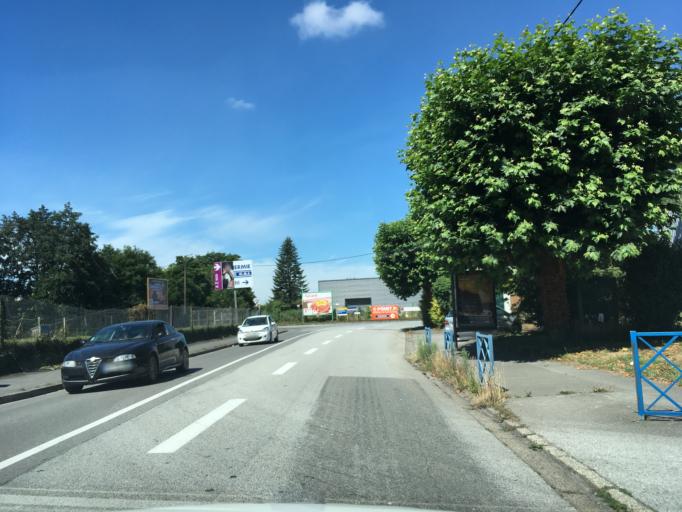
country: FR
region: Brittany
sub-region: Departement du Finistere
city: Quimper
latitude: 47.9951
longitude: -4.0746
